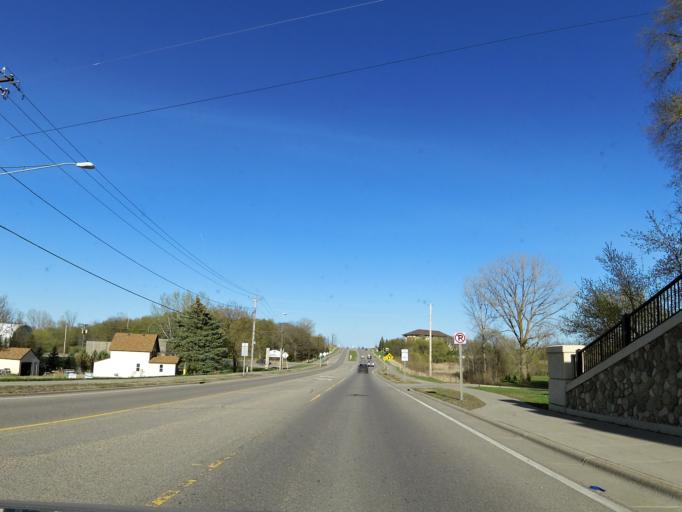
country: US
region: Minnesota
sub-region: Scott County
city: Elko New Market
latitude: 44.5730
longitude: -93.3503
